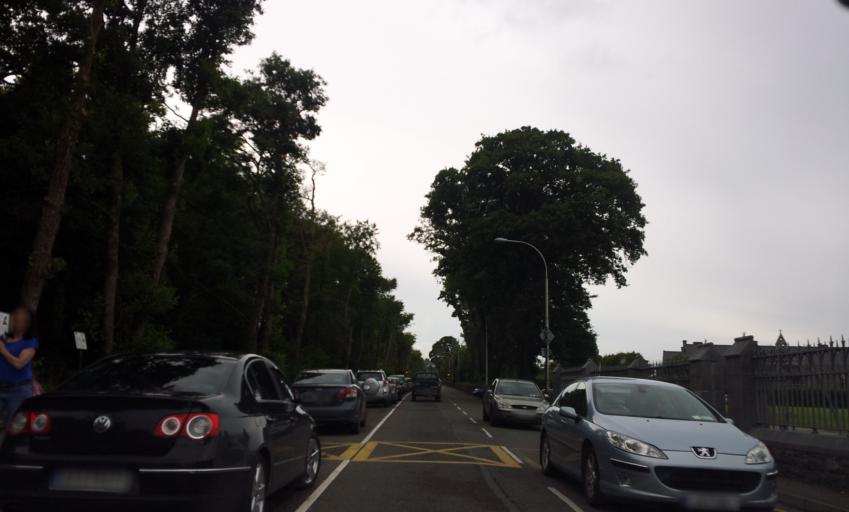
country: IE
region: Munster
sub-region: Ciarrai
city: Cill Airne
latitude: 52.0596
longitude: -9.5194
